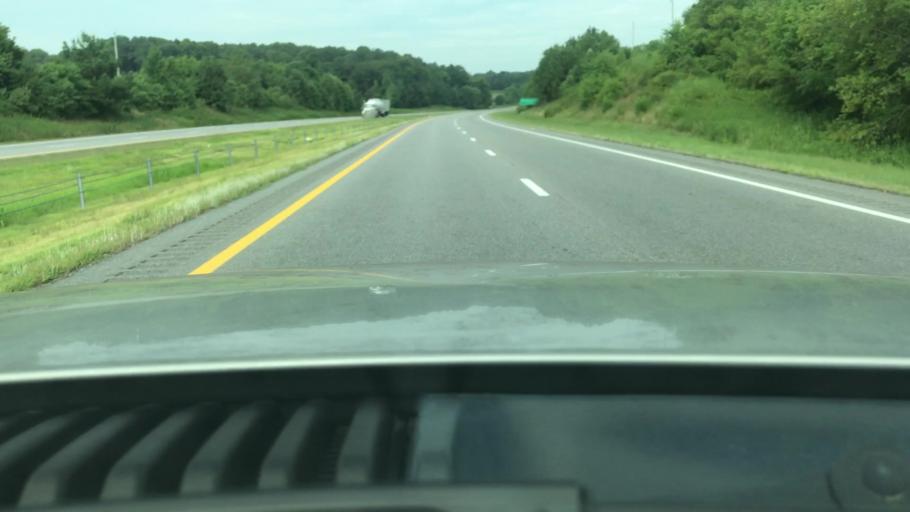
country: US
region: North Carolina
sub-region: Surry County
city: Elkin
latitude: 36.1603
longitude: -80.9626
